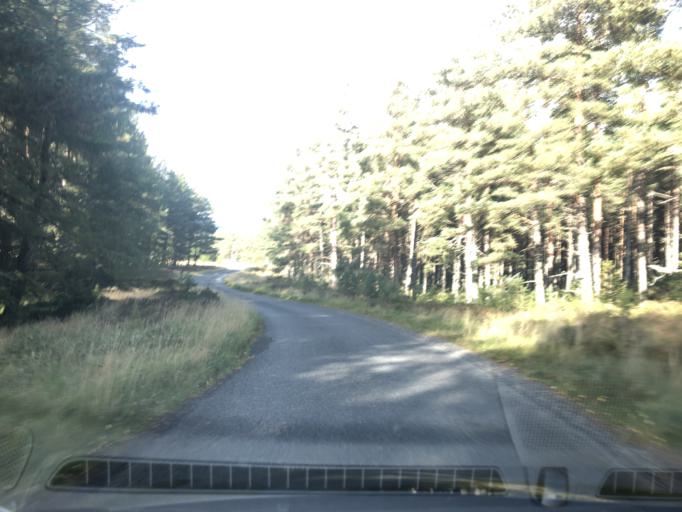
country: GB
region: Scotland
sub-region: Highland
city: Aviemore
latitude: 57.0941
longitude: -3.8919
